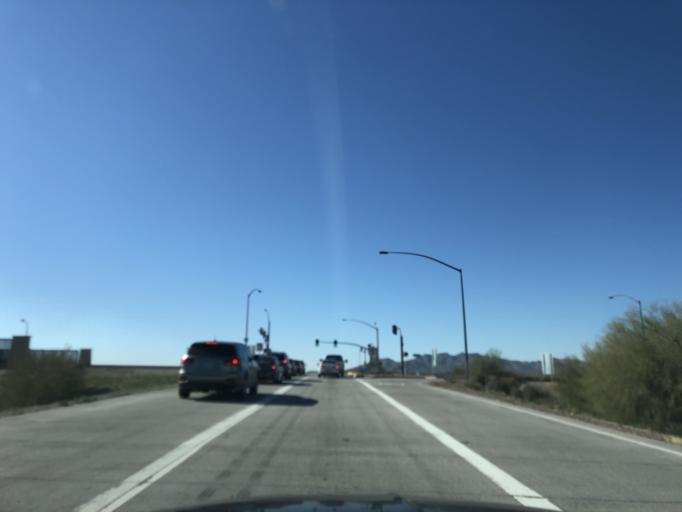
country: US
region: Arizona
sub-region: Maricopa County
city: Citrus Park
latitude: 33.4622
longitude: -112.5033
